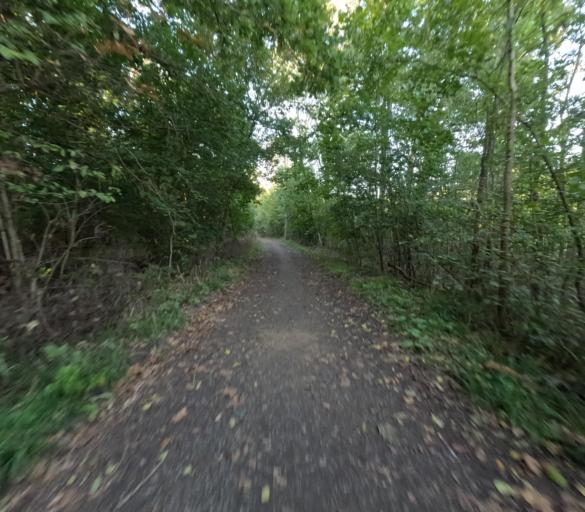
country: DE
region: Saxony
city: Schkeuditz
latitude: 51.3688
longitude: 12.2329
